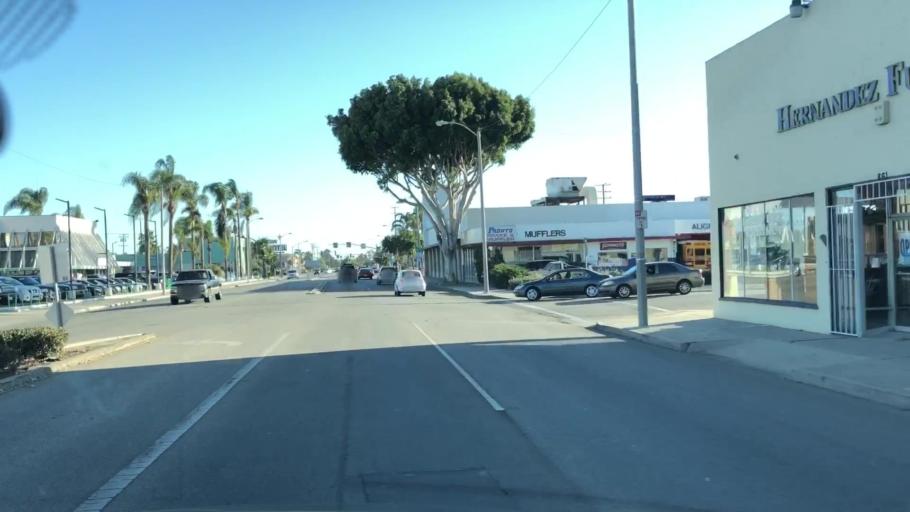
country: US
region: California
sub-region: Ventura County
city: Oxnard
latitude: 34.1927
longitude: -119.1775
